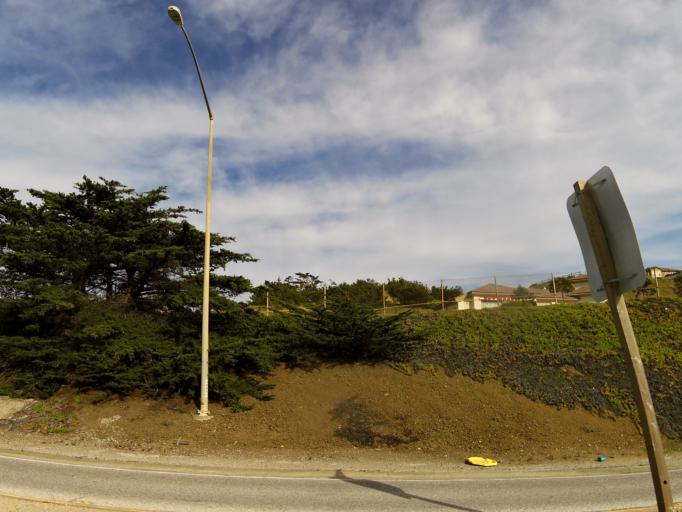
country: US
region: California
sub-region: San Mateo County
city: Pacifica
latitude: 37.6452
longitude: -122.4918
